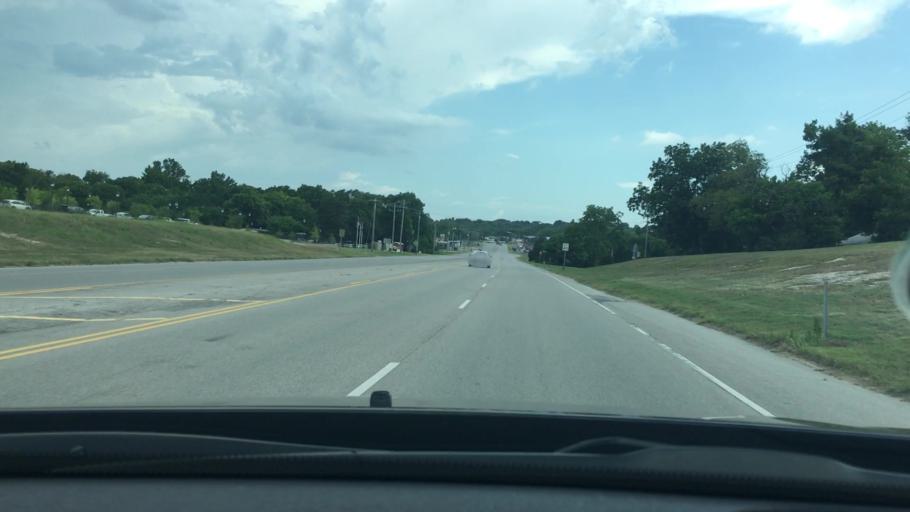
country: US
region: Oklahoma
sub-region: Pontotoc County
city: Ada
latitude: 34.7554
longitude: -96.6589
